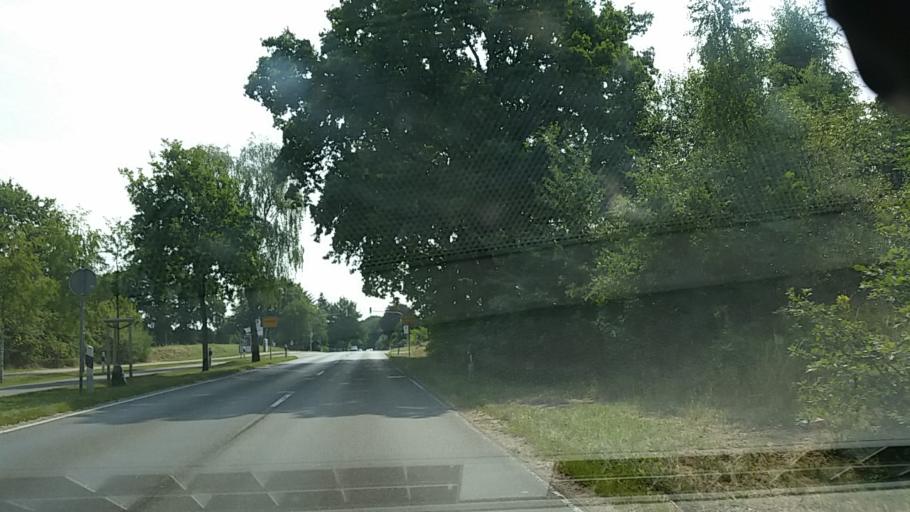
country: DE
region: Schleswig-Holstein
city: Glinde
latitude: 53.5419
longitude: 10.1855
